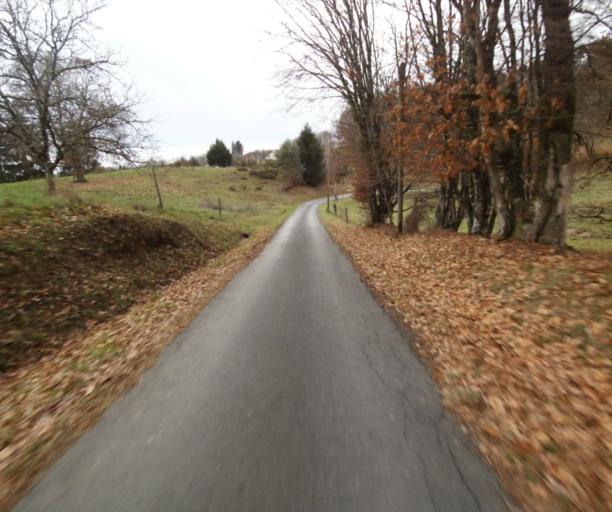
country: FR
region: Limousin
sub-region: Departement de la Correze
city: Cornil
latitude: 45.2265
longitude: 1.6701
